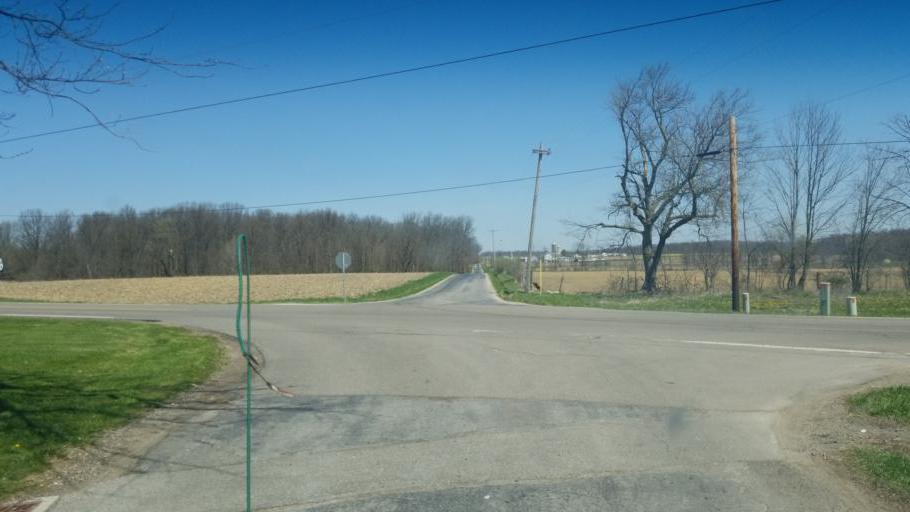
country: US
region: Ohio
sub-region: Richland County
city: Lincoln Heights
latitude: 40.8950
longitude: -82.4554
